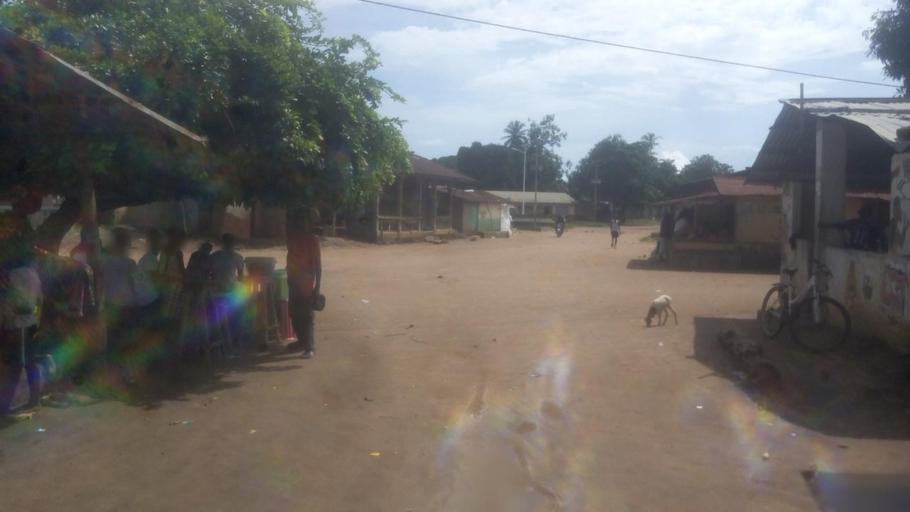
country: SL
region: Northern Province
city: Tintafor
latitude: 8.6412
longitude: -13.2264
